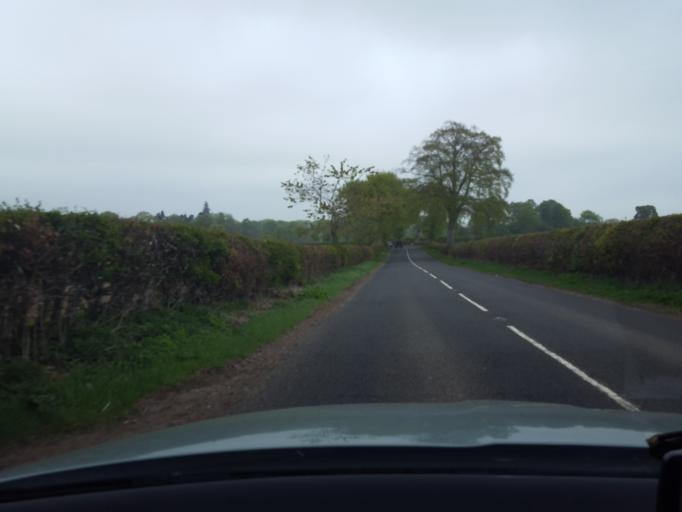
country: GB
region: Scotland
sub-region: Angus
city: Brechin
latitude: 56.7627
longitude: -2.6450
